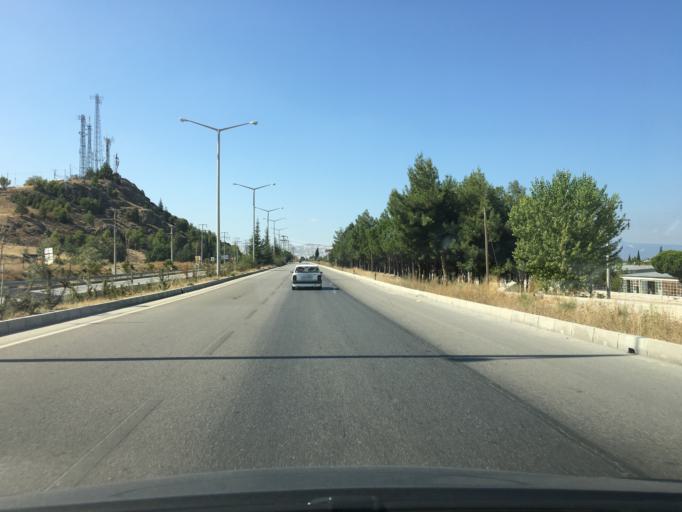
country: TR
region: Burdur
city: Burdur
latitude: 37.7460
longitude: 30.3187
